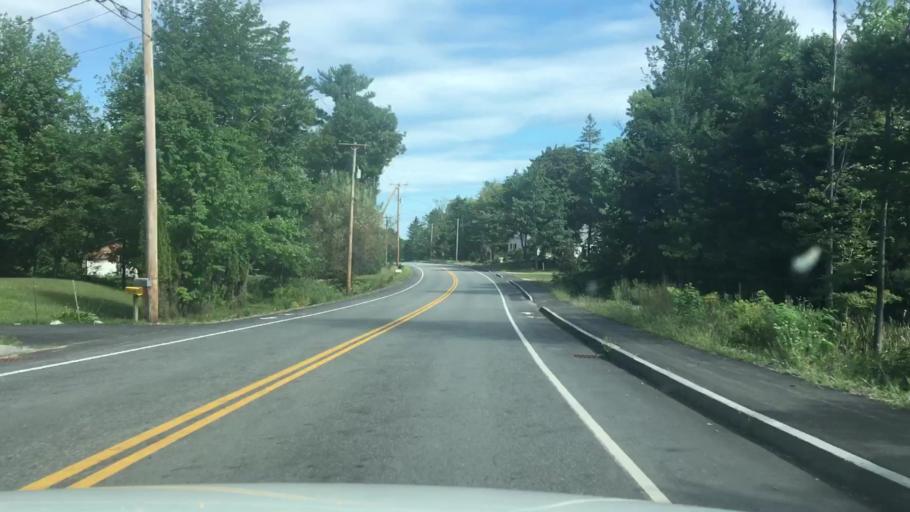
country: US
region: Maine
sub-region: Androscoggin County
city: Auburn
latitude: 44.1159
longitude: -70.2504
